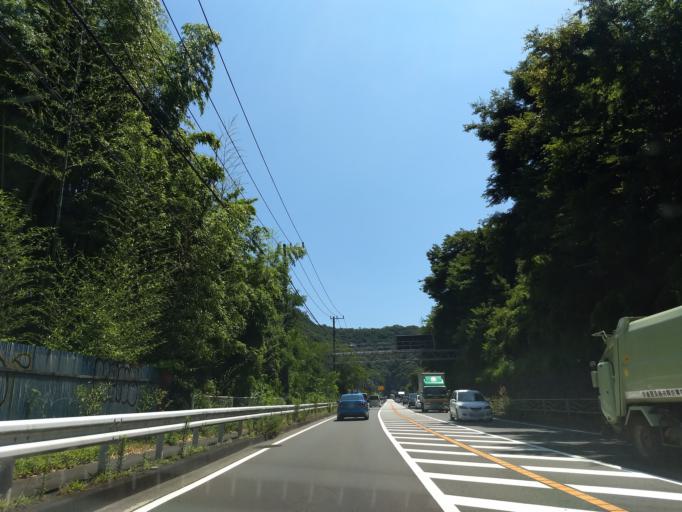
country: JP
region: Kanagawa
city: Hadano
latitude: 35.3836
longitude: 139.2448
